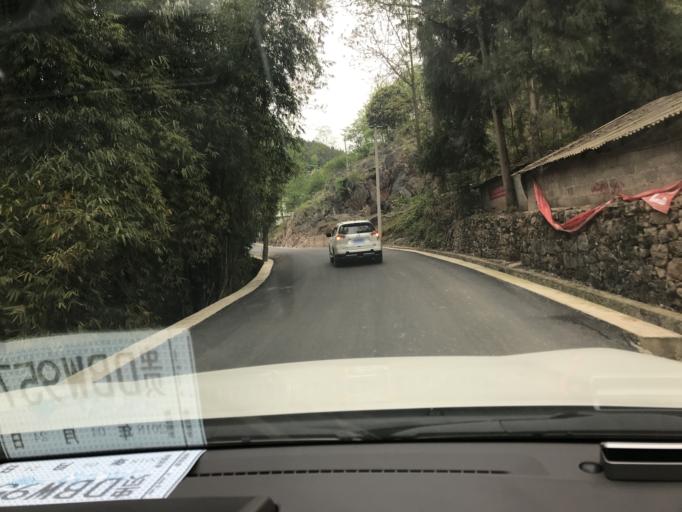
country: CN
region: Guizhou Sheng
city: Tongjing
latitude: 28.3063
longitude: 108.2648
